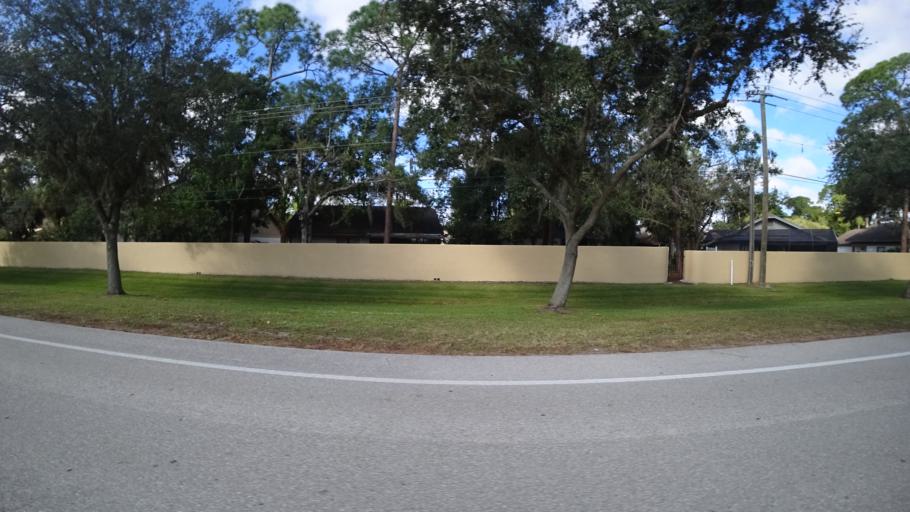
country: US
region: Florida
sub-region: Sarasota County
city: Desoto Lakes
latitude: 27.4007
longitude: -82.4871
